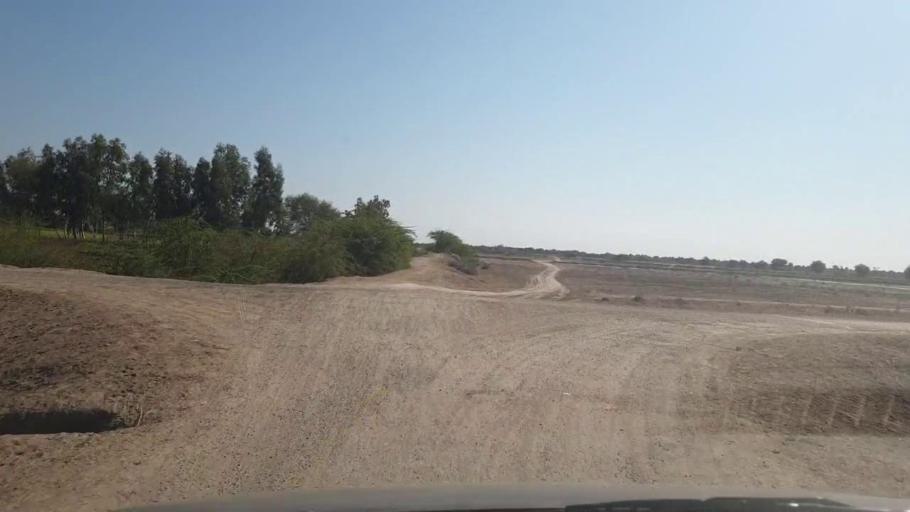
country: PK
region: Sindh
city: Dhoro Naro
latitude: 25.3982
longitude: 69.5875
